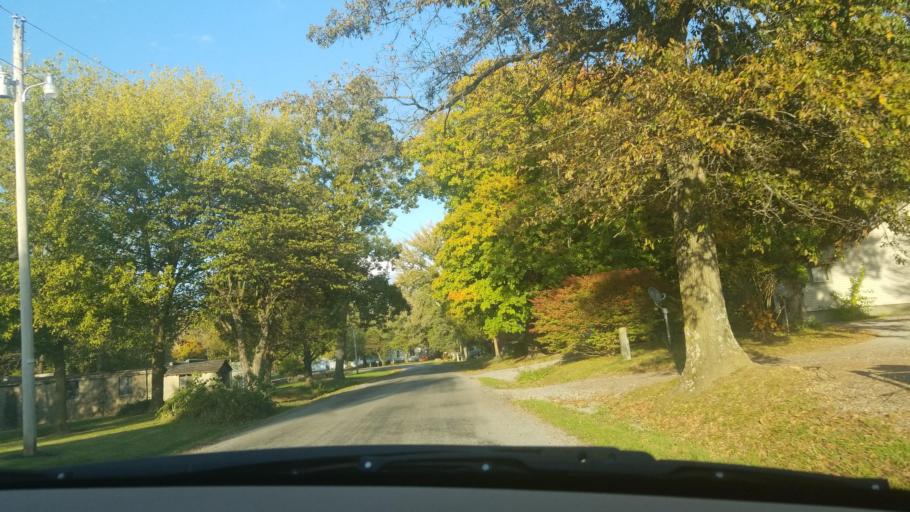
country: US
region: Illinois
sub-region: Williamson County
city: Johnston City
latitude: 37.7674
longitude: -88.7734
